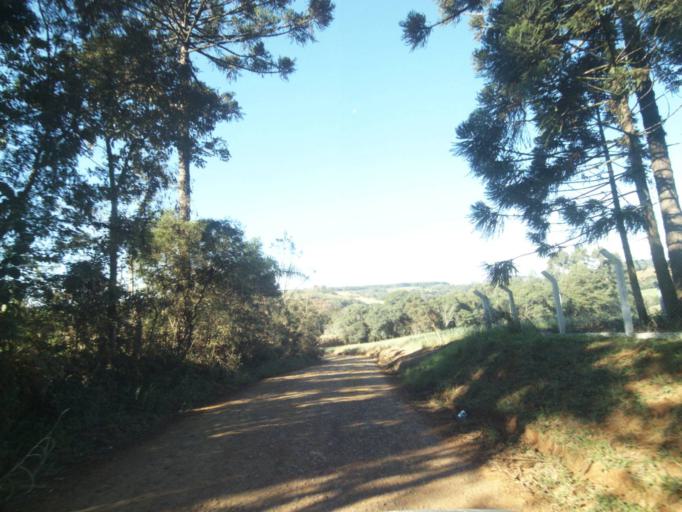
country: BR
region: Parana
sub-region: Tibagi
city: Tibagi
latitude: -24.5348
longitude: -50.4950
